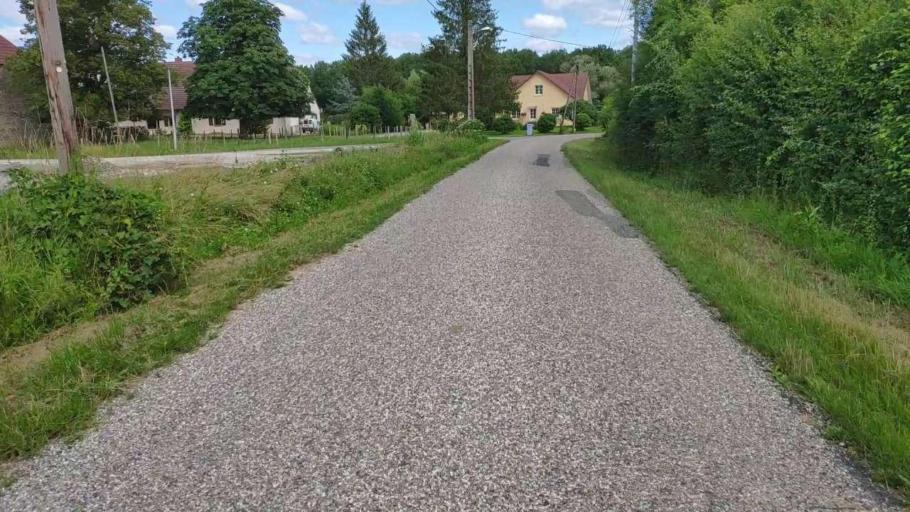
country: FR
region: Franche-Comte
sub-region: Departement du Jura
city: Bletterans
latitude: 46.8206
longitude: 5.4496
